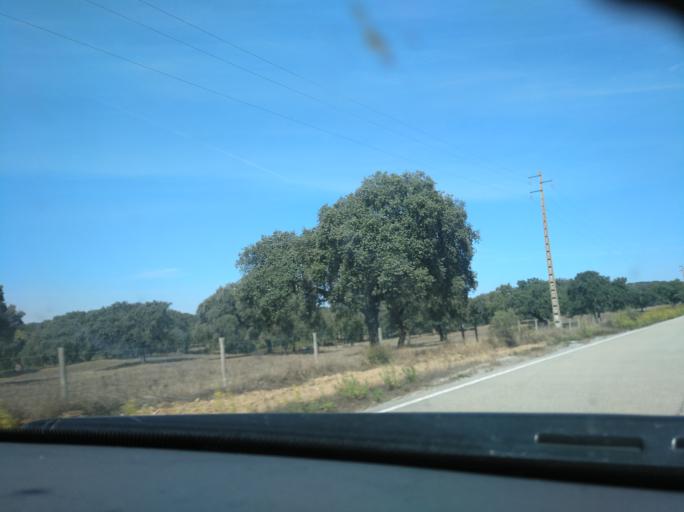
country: PT
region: Evora
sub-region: Arraiolos
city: Arraiolos
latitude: 38.6832
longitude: -8.0916
